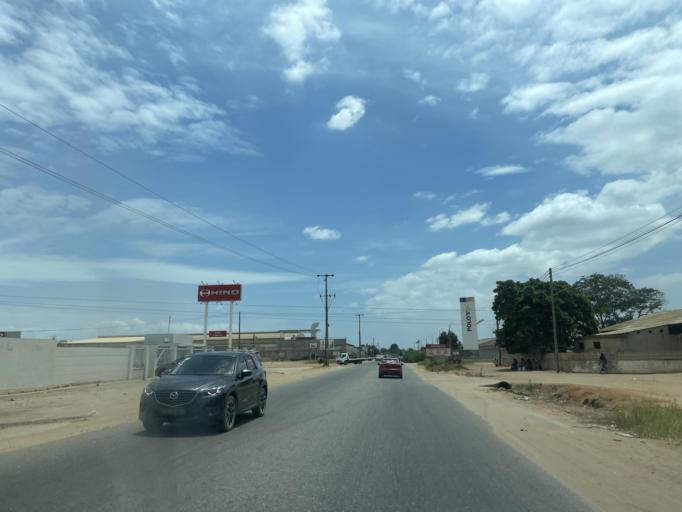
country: AO
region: Luanda
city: Luanda
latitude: -8.9276
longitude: 13.3961
